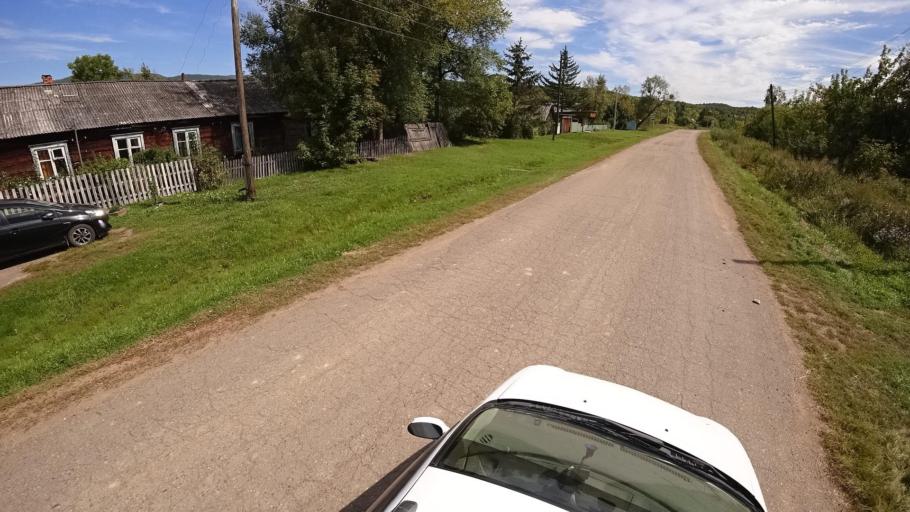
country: RU
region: Primorskiy
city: Yakovlevka
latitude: 44.6562
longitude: 133.7422
